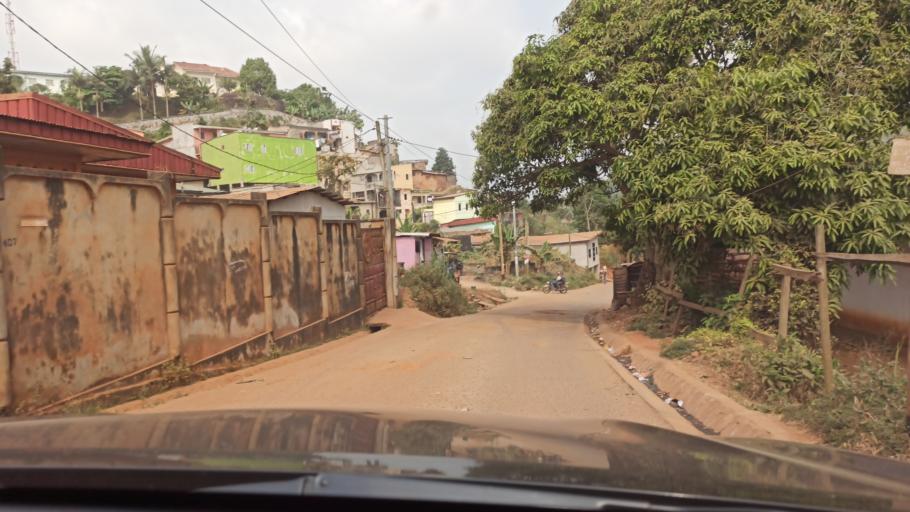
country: CM
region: Centre
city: Yaounde
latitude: 3.8778
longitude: 11.4808
